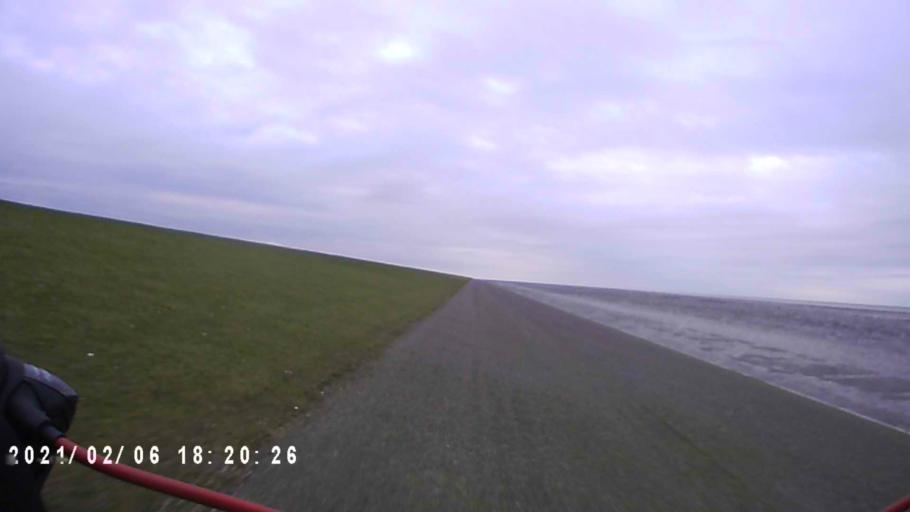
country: DE
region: Lower Saxony
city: Borkum
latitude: 53.4646
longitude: 6.7292
